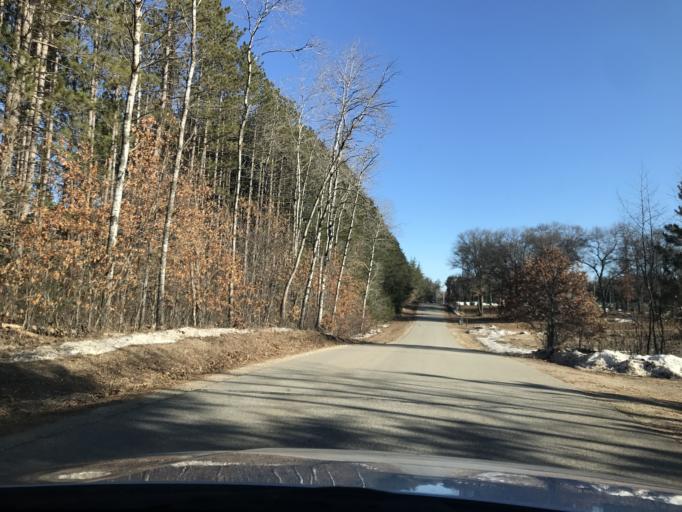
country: US
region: Wisconsin
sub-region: Marinette County
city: Niagara
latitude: 45.3949
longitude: -88.0791
